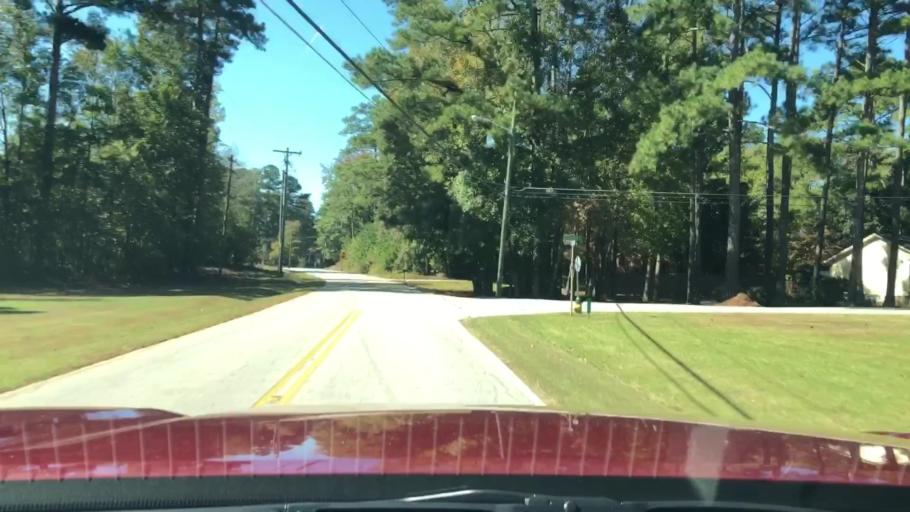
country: US
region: South Carolina
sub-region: Greenwood County
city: Greenwood
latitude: 34.2256
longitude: -82.1541
